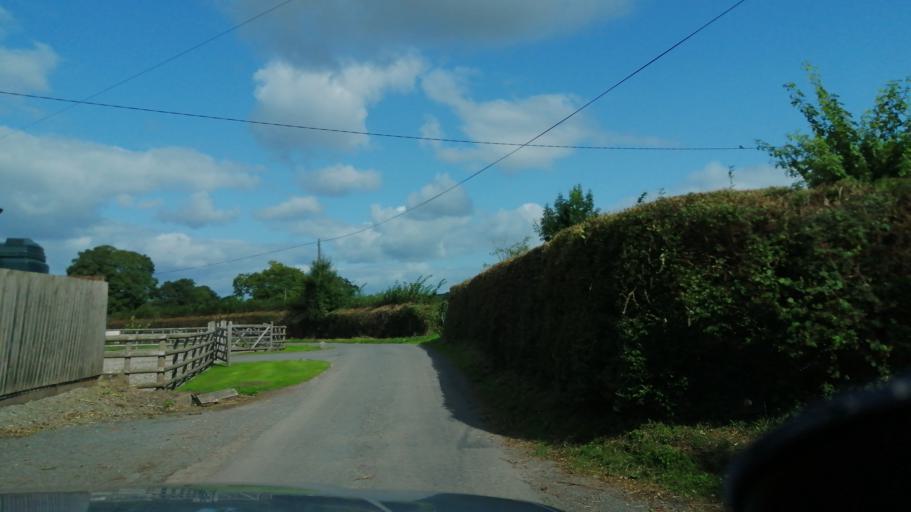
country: GB
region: England
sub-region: Herefordshire
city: Kinnersley
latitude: 52.1260
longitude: -2.9243
